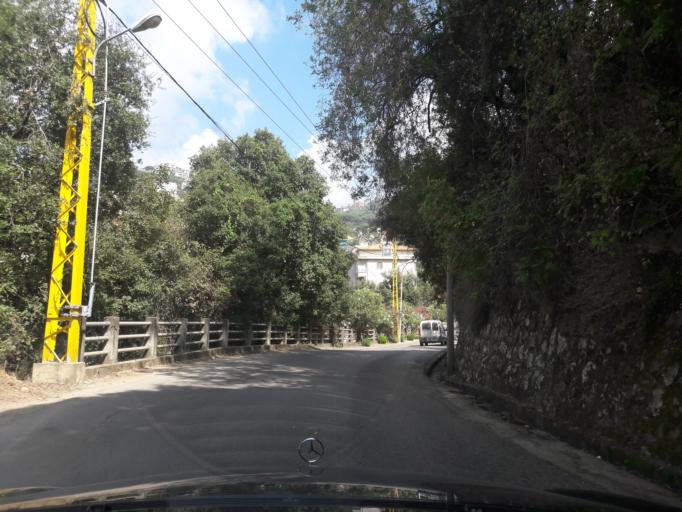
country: LB
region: Mont-Liban
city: Djounie
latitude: 33.9262
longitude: 35.6671
